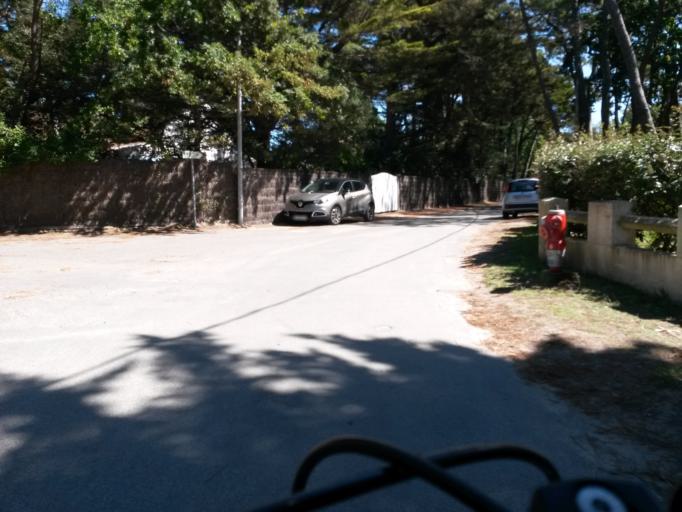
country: FR
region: Pays de la Loire
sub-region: Departement de la Loire-Atlantique
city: Mesquer
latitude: 47.4061
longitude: -2.4882
